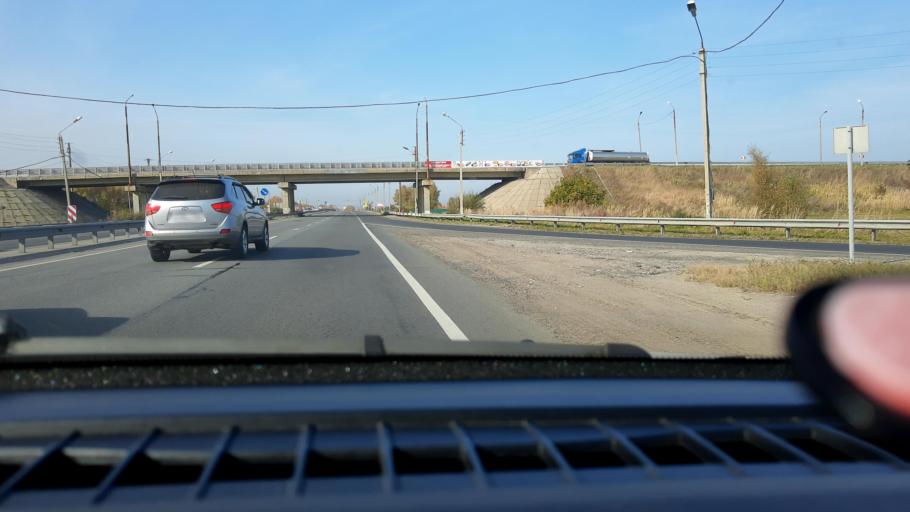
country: RU
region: Nizjnij Novgorod
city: Kstovo
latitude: 56.1272
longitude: 44.2614
